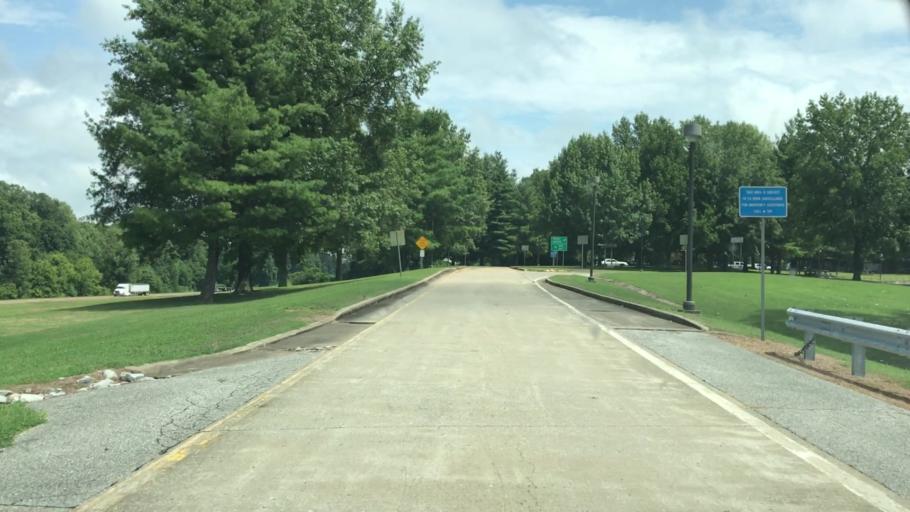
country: US
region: Tennessee
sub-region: Dyer County
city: Dyersburg
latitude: 36.0719
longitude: -89.4716
